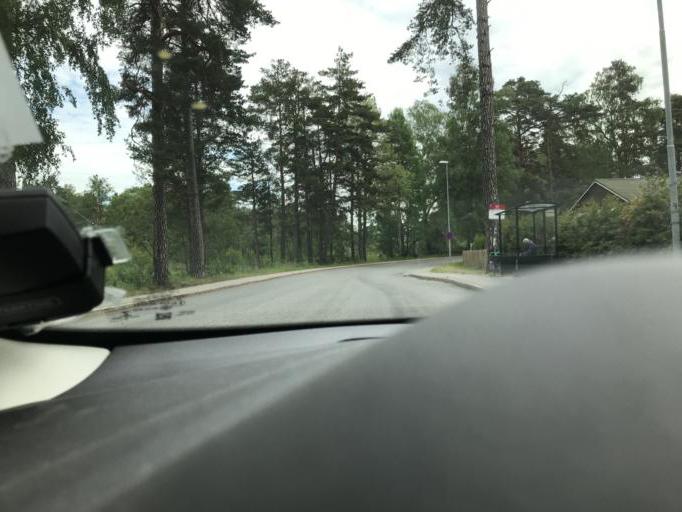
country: SE
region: Stockholm
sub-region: Botkyrka Kommun
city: Varsta
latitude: 59.1969
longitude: 17.8011
